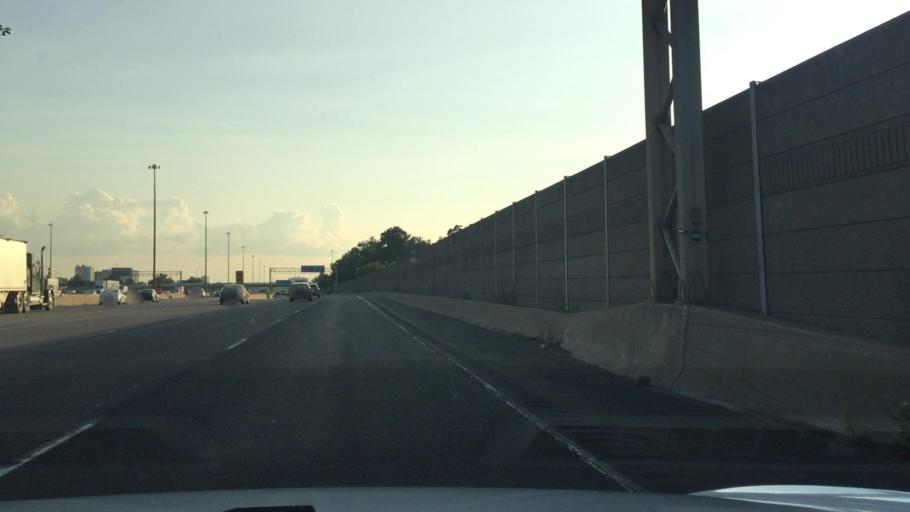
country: CA
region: Ontario
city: Scarborough
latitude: 43.7755
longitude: -79.2993
